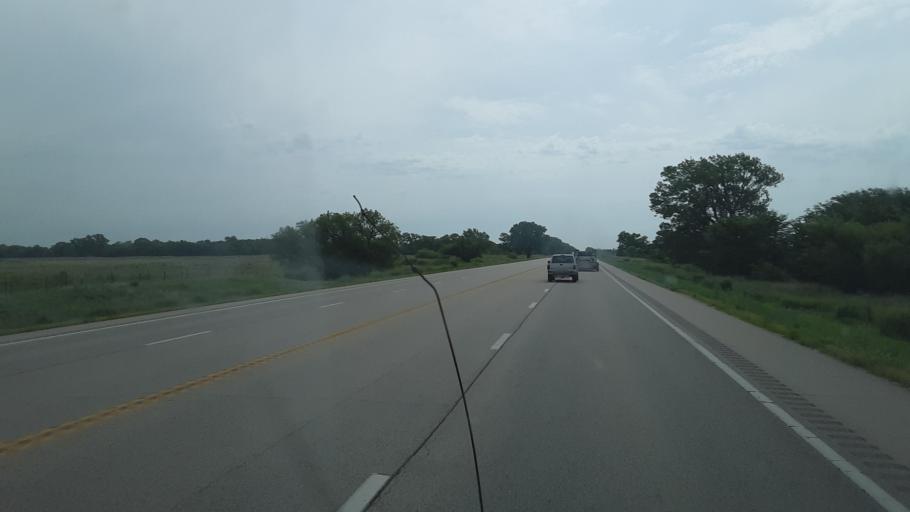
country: US
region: Kansas
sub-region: Rice County
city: Sterling
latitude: 37.9846
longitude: -98.2964
